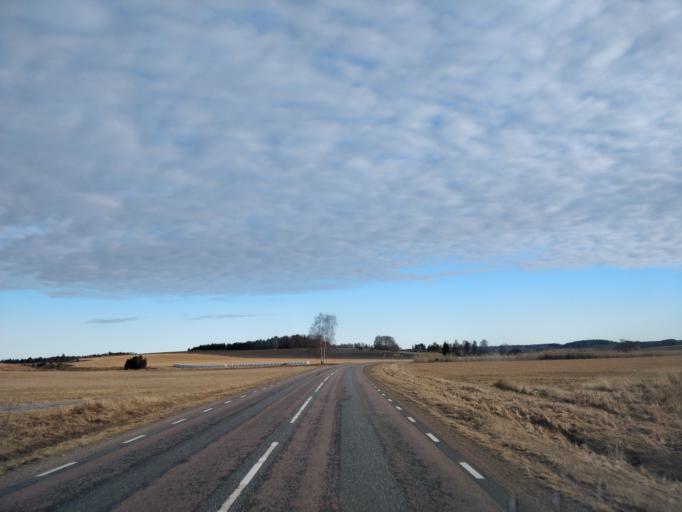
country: SE
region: Uppsala
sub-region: Enkopings Kommun
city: Enkoping
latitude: 59.7827
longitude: 17.0857
